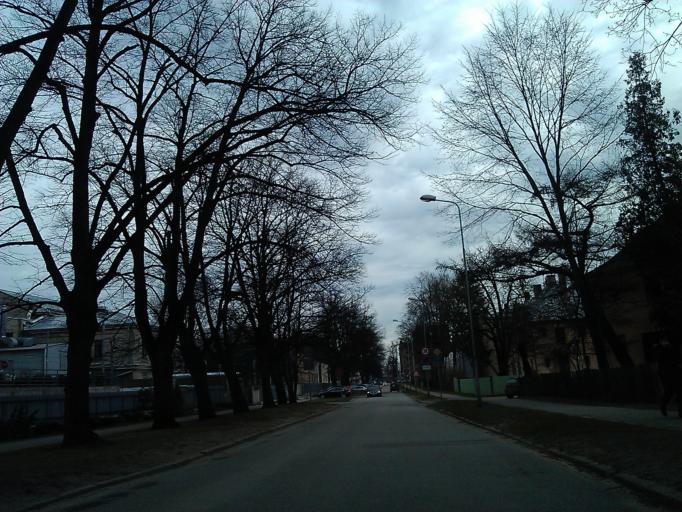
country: LV
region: Riga
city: Riga
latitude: 56.9728
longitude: 24.1480
